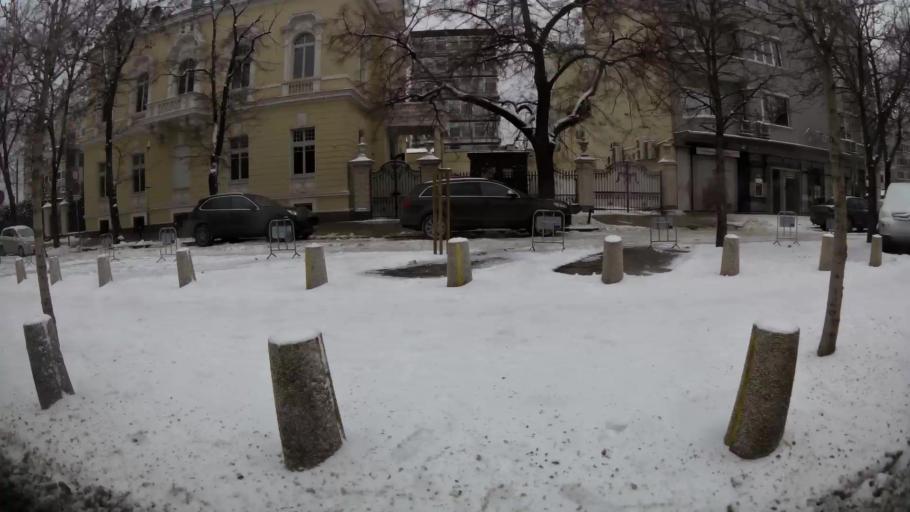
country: BG
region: Sofia-Capital
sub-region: Stolichna Obshtina
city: Sofia
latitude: 42.6934
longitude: 23.3333
